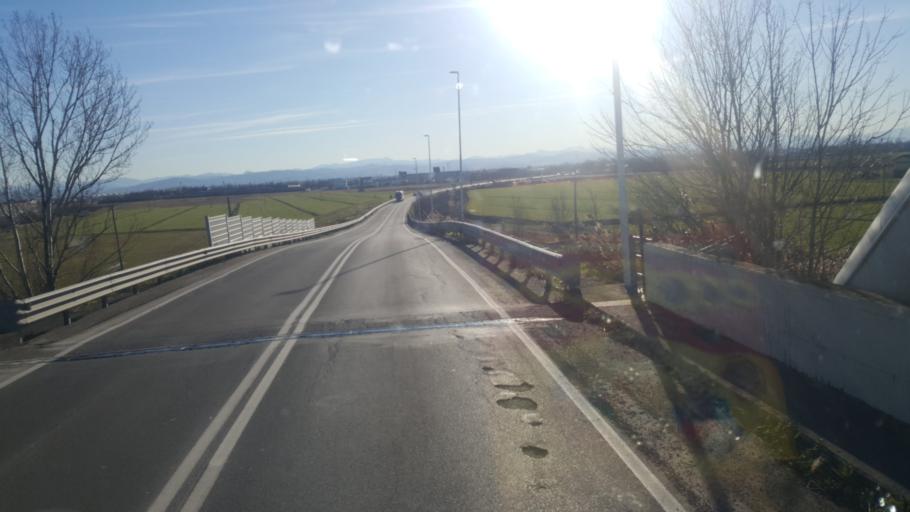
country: IT
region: Emilia-Romagna
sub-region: Provincia di Reggio Emilia
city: Bagnolo in Piano
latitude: 44.7561
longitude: 10.6578
